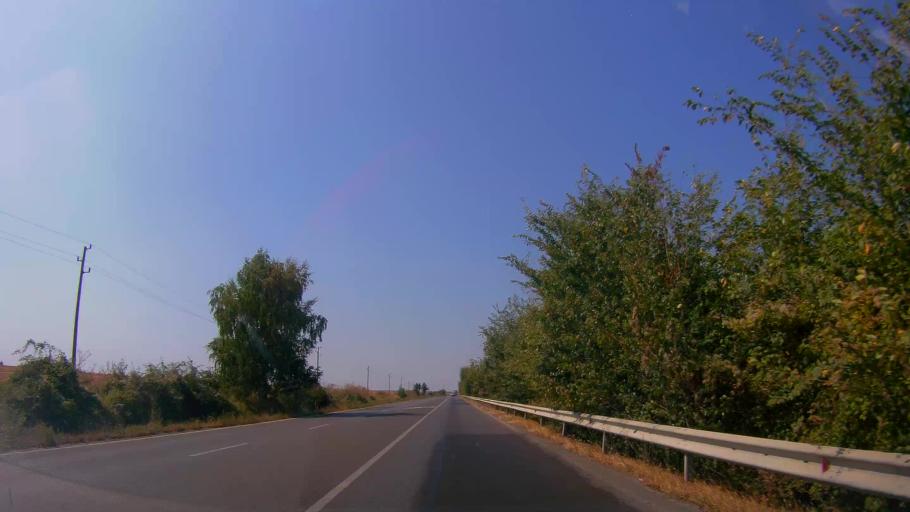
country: BG
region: Ruse
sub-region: Obshtina Vetovo
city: Senovo
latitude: 43.5620
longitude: 26.3511
